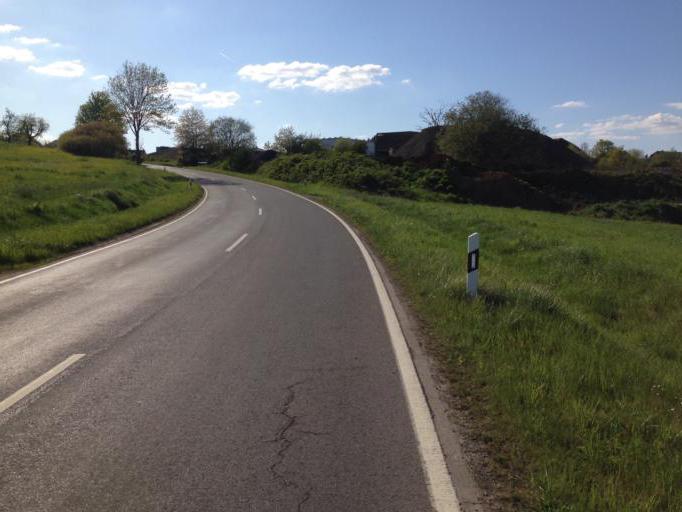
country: DE
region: Hesse
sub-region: Regierungsbezirk Giessen
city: Reiskirchen
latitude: 50.5755
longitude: 8.8270
